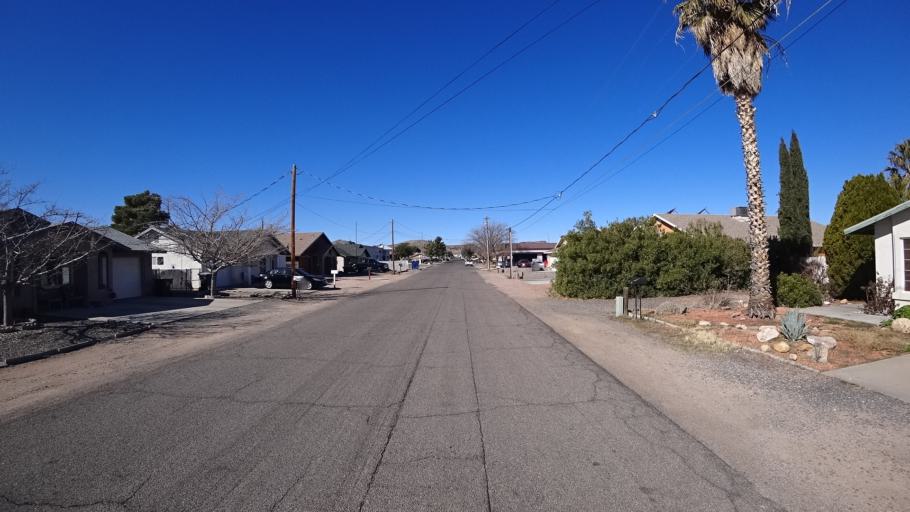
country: US
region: Arizona
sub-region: Mohave County
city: Kingman
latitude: 35.2082
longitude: -114.0330
